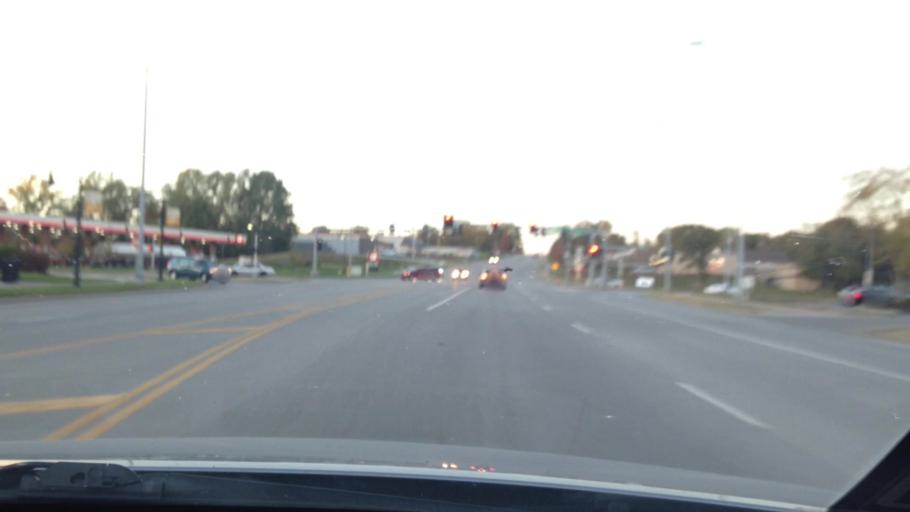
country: US
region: Missouri
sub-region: Platte County
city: Riverside
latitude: 39.1768
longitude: -94.6132
